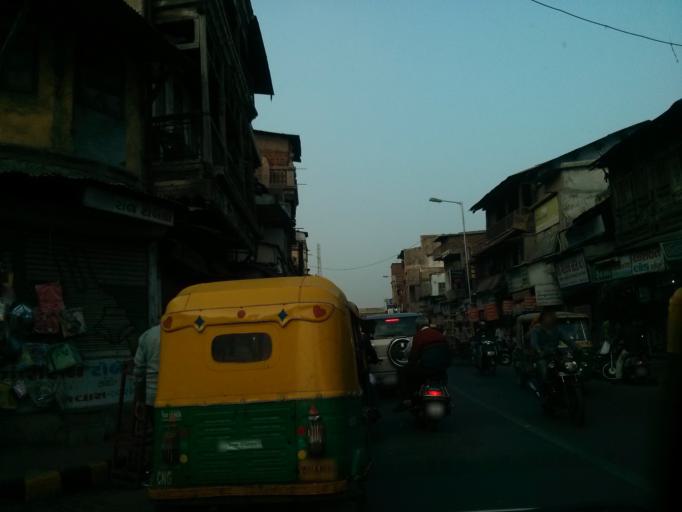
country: IN
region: Gujarat
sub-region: Ahmadabad
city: Ahmedabad
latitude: 23.0365
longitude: 72.5877
